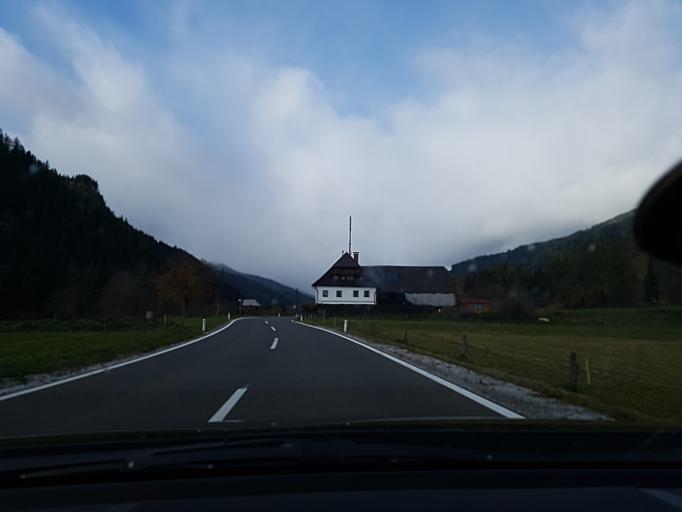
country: AT
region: Styria
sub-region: Politischer Bezirk Murtal
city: Sankt Johann am Tauern
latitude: 47.3037
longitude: 14.4871
